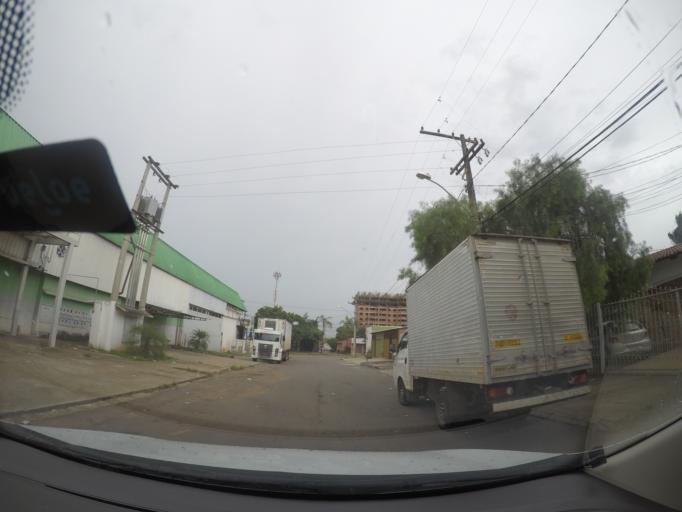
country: BR
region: Goias
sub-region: Goiania
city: Goiania
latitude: -16.6977
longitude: -49.3137
